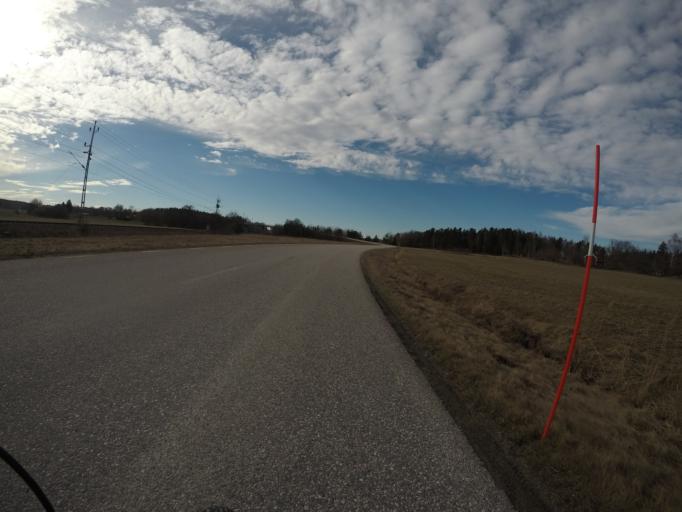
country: SE
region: Vaestmanland
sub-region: Kungsors Kommun
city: Kungsoer
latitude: 59.4206
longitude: 16.1706
